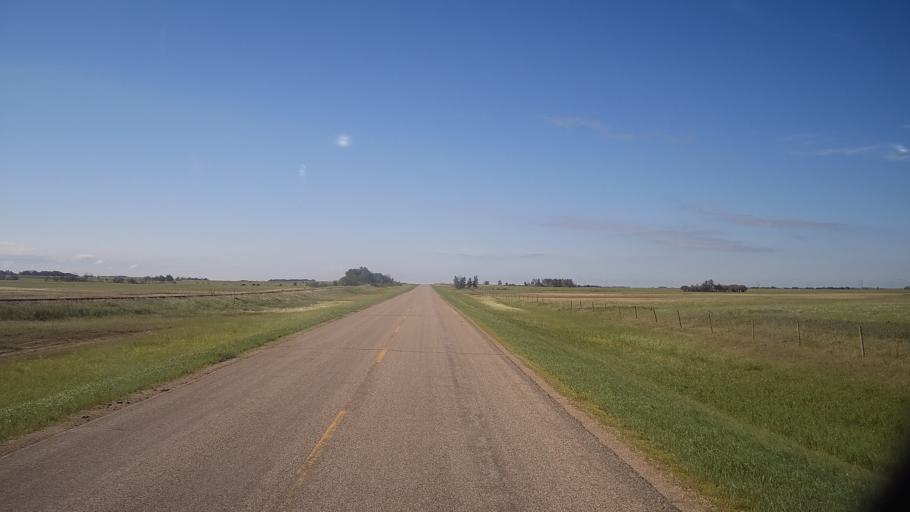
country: CA
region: Saskatchewan
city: Watrous
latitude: 51.7546
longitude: -105.2867
